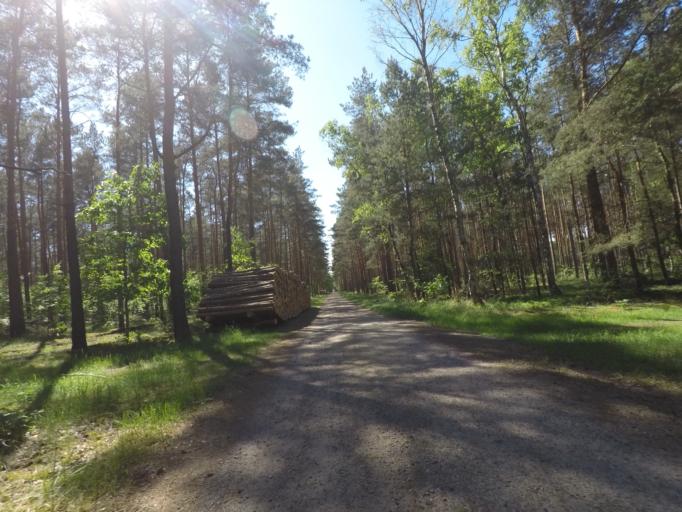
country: DE
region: Brandenburg
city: Melchow
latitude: 52.8278
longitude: 13.7427
